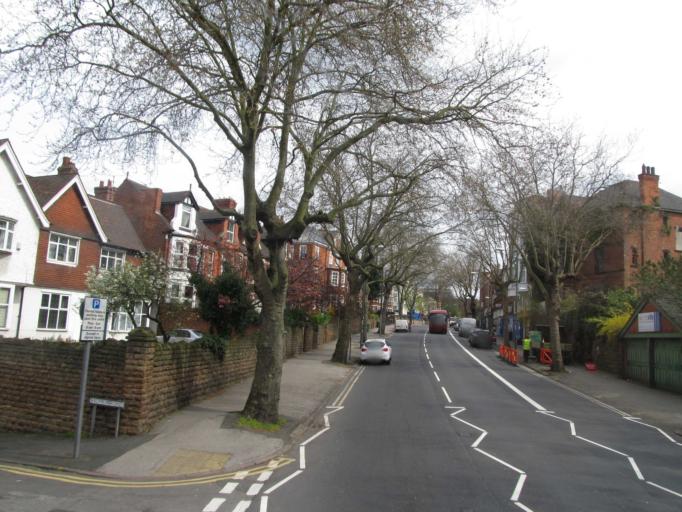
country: GB
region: England
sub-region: Nottingham
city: Nottingham
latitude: 52.9540
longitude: -1.1689
